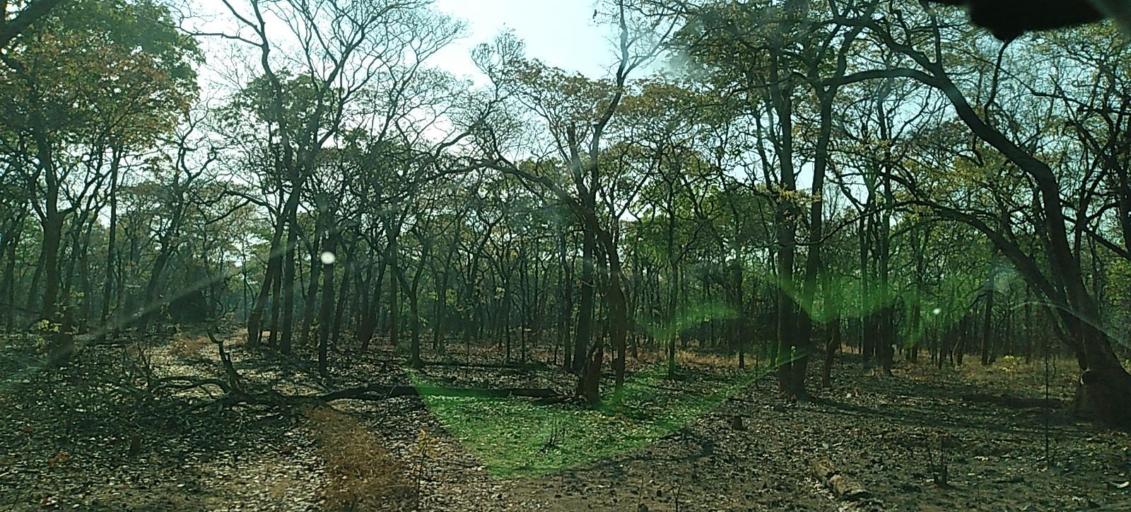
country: ZM
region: North-Western
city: Kalengwa
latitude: -13.2284
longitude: 25.0823
